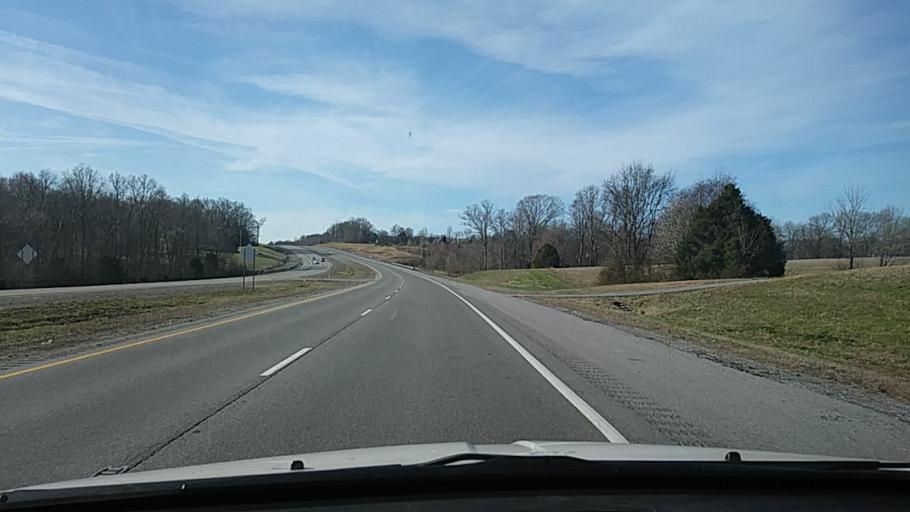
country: US
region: Tennessee
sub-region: Sumner County
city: Portland
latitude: 36.5399
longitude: -86.5072
